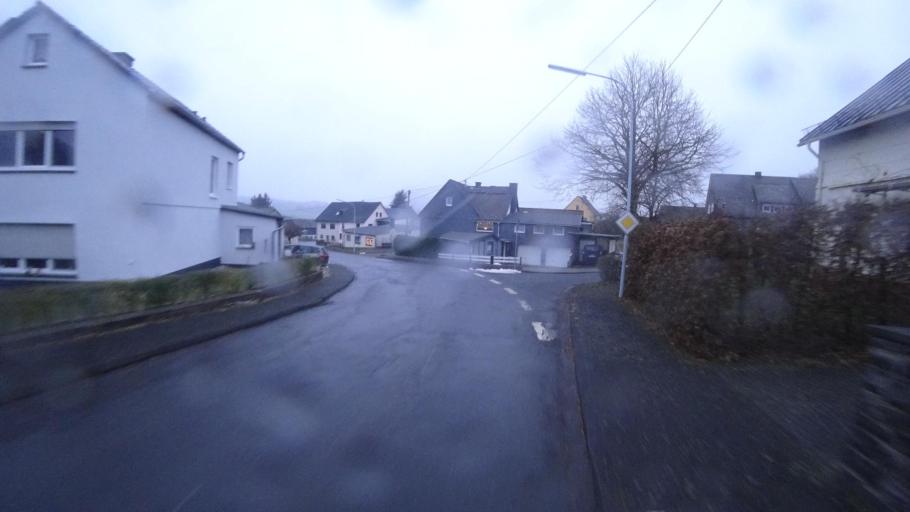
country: DE
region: Rheinland-Pfalz
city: Enspel
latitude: 50.6163
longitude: 7.8858
